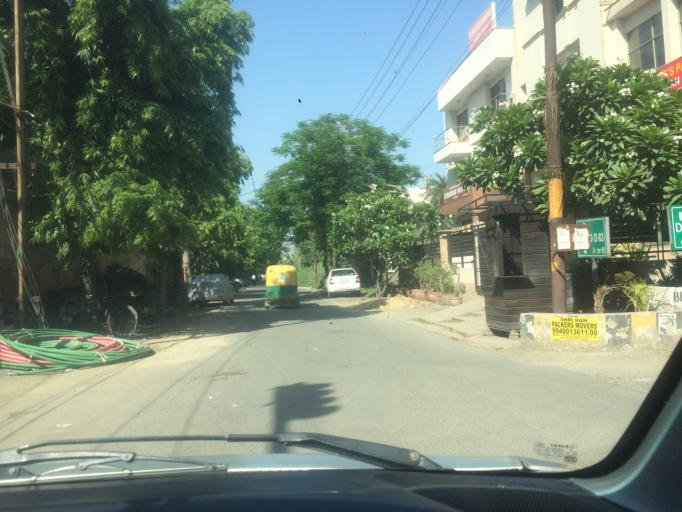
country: IN
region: Uttar Pradesh
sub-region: Gautam Buddha Nagar
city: Noida
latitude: 28.5781
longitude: 77.3377
